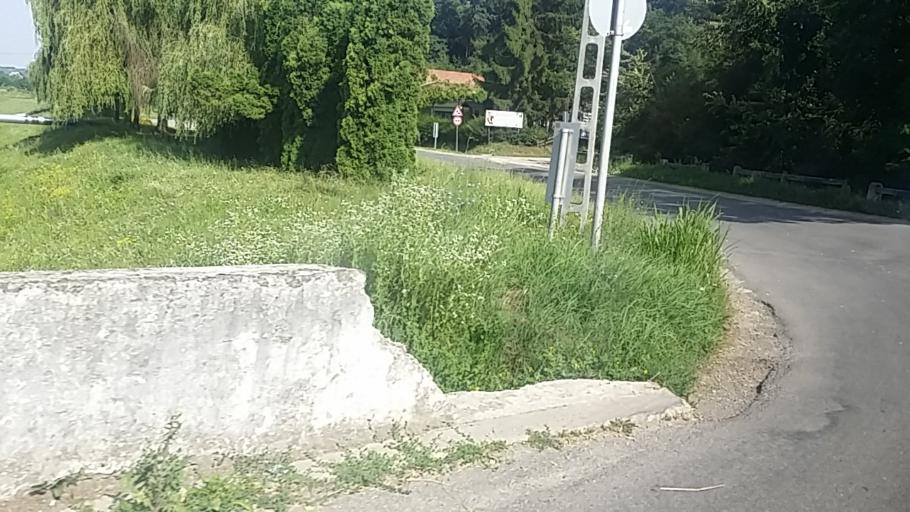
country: HU
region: Baranya
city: Villany
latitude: 45.8770
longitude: 18.4458
